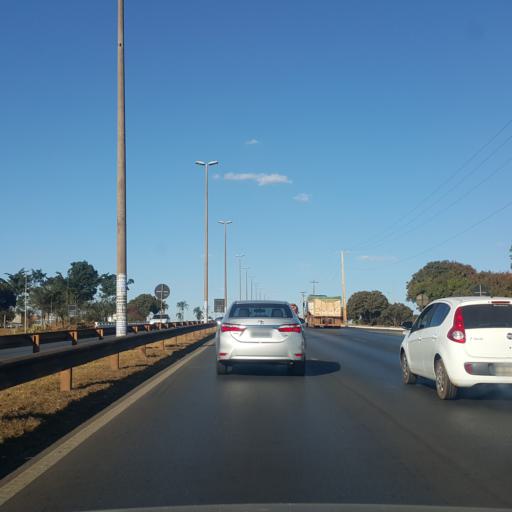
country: BR
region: Federal District
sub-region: Brasilia
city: Brasilia
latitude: -15.7862
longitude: -47.9984
